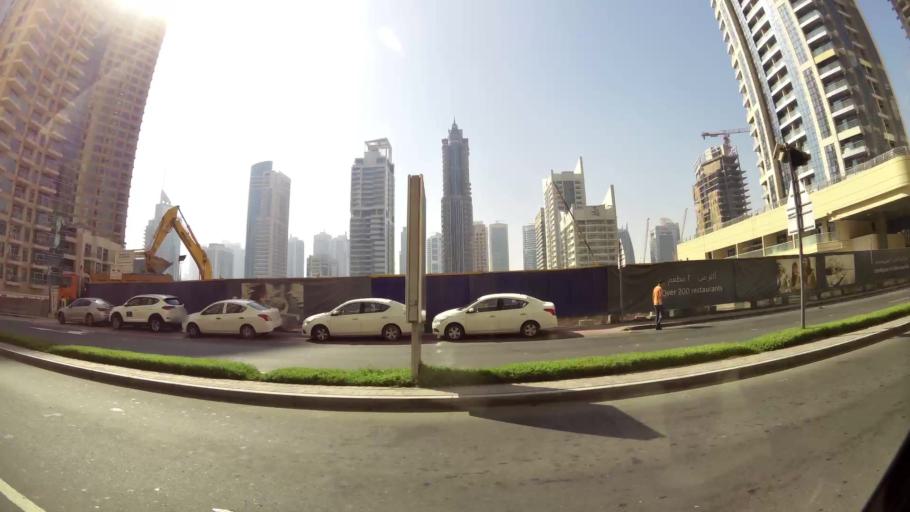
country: AE
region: Dubai
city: Dubai
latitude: 25.0813
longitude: 55.1405
